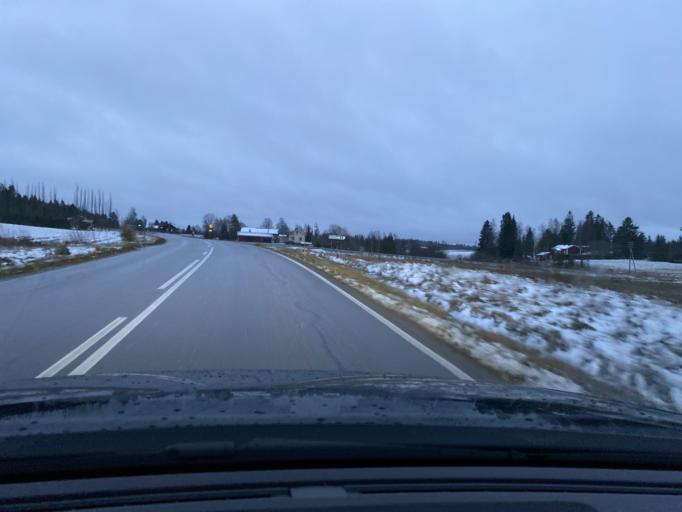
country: FI
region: Pirkanmaa
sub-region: Lounais-Pirkanmaa
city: Punkalaidun
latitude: 61.1236
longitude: 23.0280
